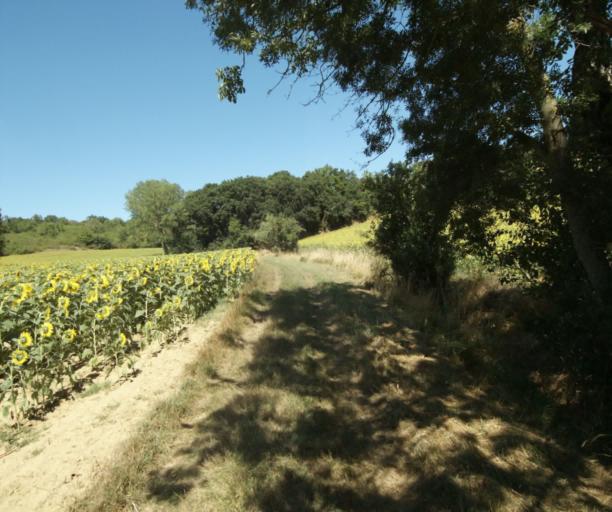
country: FR
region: Midi-Pyrenees
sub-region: Departement de la Haute-Garonne
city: Auriac-sur-Vendinelle
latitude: 43.5008
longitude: 1.8697
